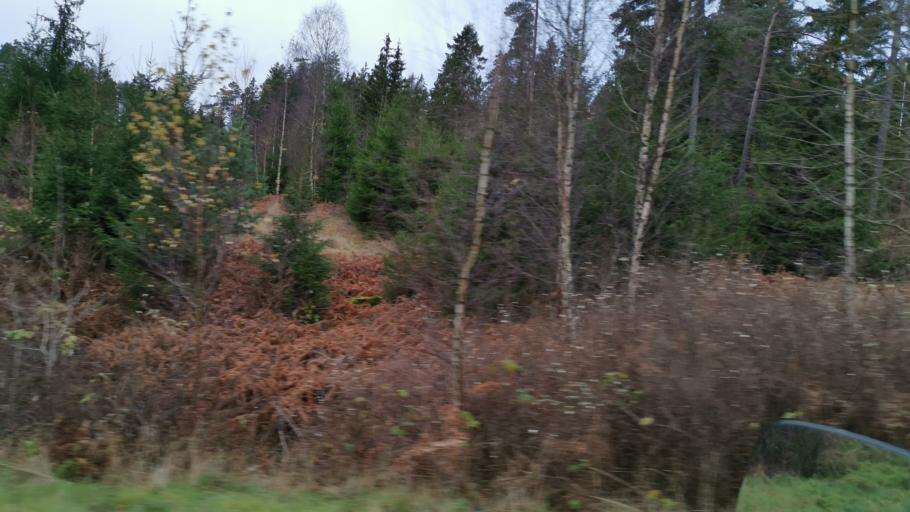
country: SE
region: Vaestra Goetaland
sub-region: Orust
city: Henan
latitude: 58.2191
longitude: 11.7113
